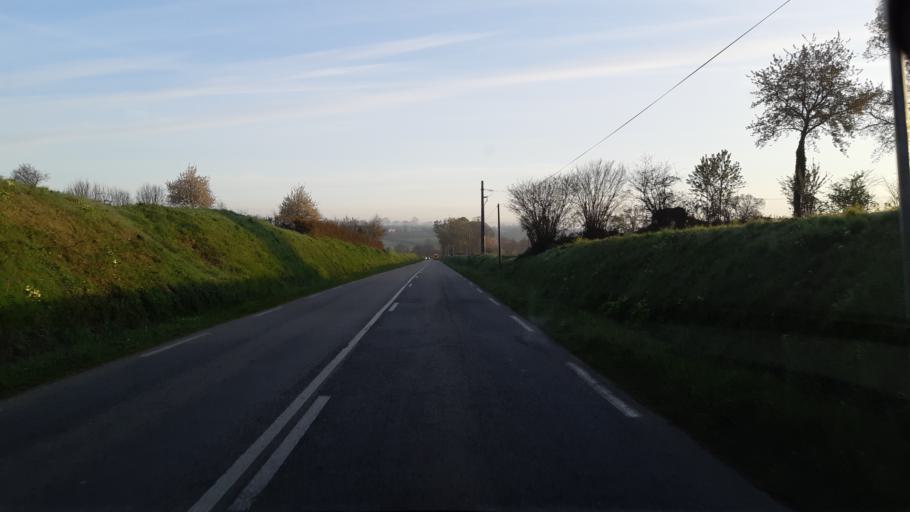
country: FR
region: Lower Normandy
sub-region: Departement de la Manche
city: Agneaux
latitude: 49.0609
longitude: -1.1330
